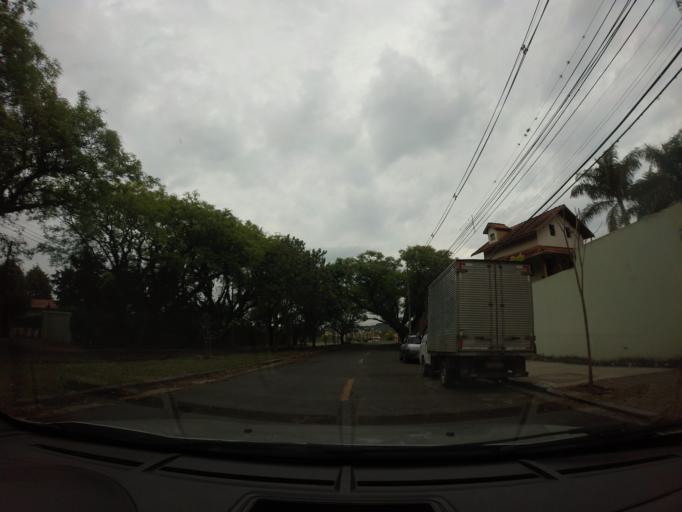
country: BR
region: Sao Paulo
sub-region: Piracicaba
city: Piracicaba
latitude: -22.7538
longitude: -47.5948
